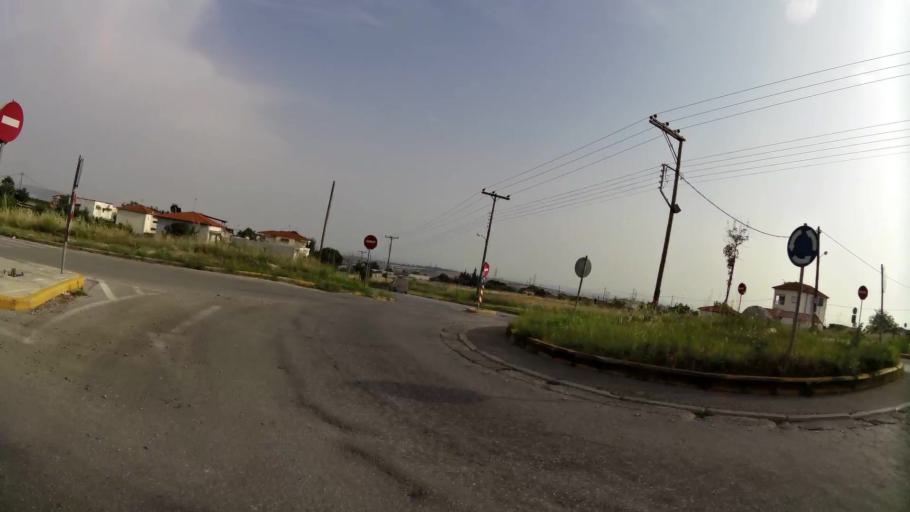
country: GR
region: Central Macedonia
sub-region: Nomos Thessalonikis
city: Oraiokastro
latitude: 40.7188
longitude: 22.9104
